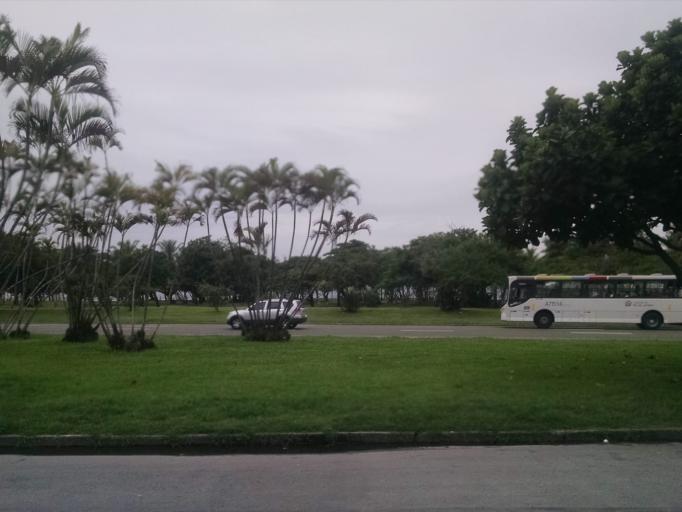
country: BR
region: Rio de Janeiro
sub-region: Rio De Janeiro
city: Rio de Janeiro
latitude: -22.9236
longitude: -43.1712
